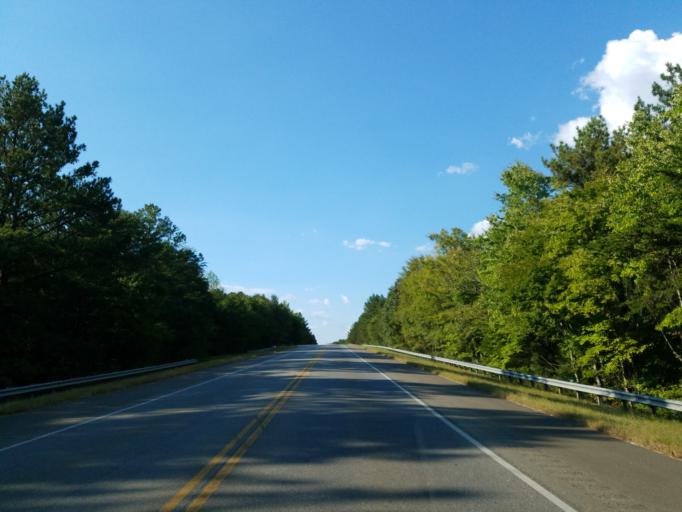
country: US
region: Georgia
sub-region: Murray County
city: Chatsworth
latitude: 34.6802
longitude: -84.7277
